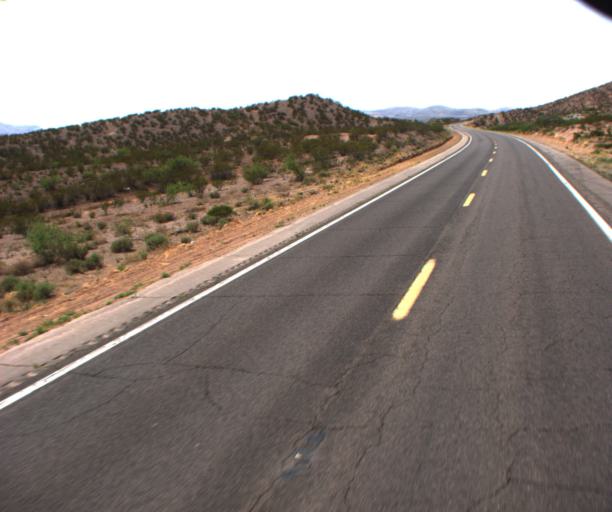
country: US
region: Arizona
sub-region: Greenlee County
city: Clifton
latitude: 32.7960
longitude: -109.1622
